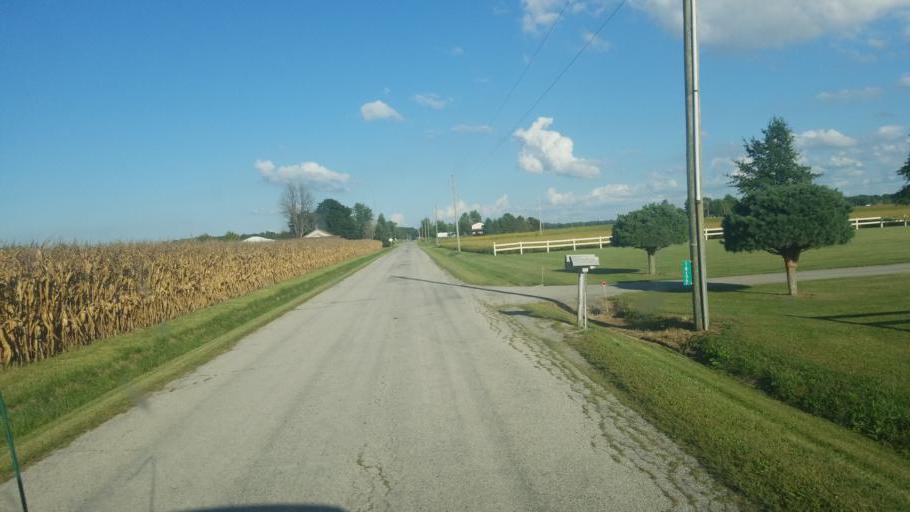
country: US
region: Ohio
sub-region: Hancock County
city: Arlington
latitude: 40.9353
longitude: -83.5721
